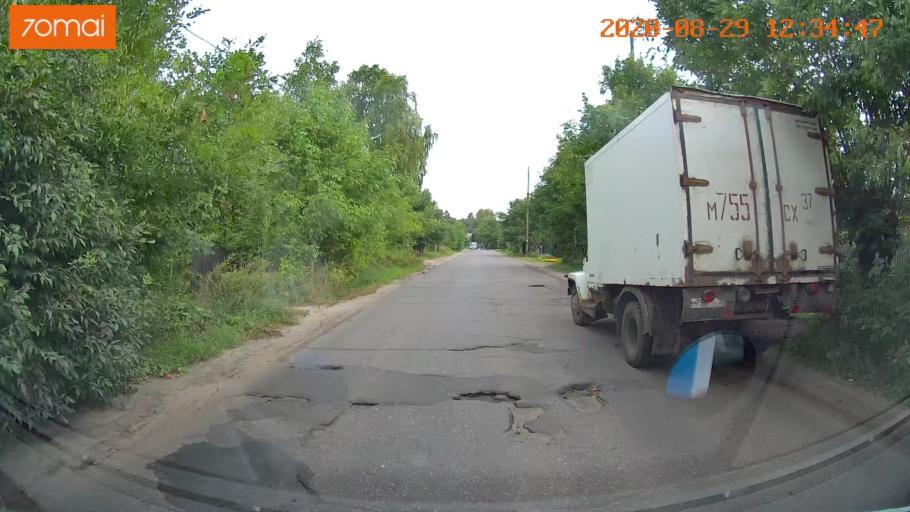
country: RU
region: Ivanovo
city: Yur'yevets
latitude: 57.3114
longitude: 43.1022
